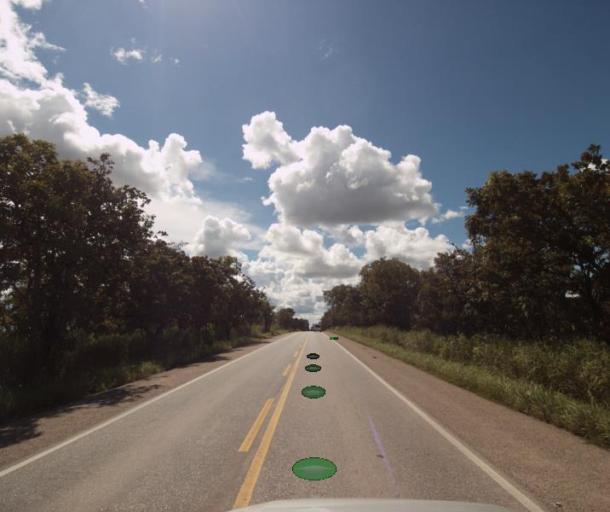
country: BR
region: Goias
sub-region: Porangatu
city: Porangatu
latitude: -13.6635
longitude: -49.0322
